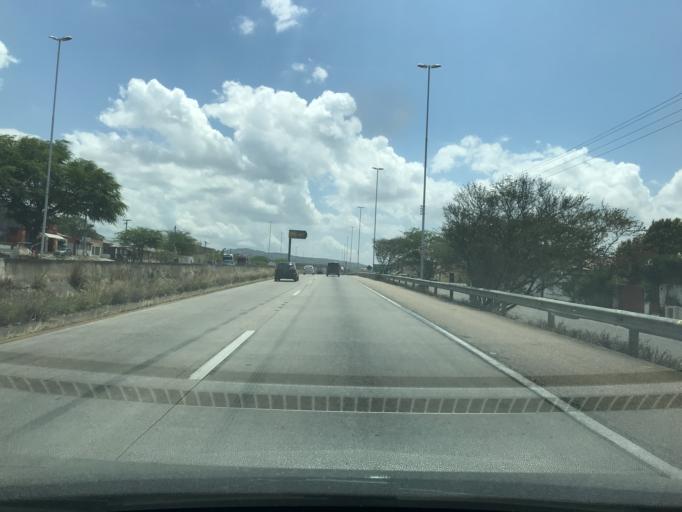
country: BR
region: Pernambuco
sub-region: Bezerros
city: Bezerros
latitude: -8.2998
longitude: -35.8433
